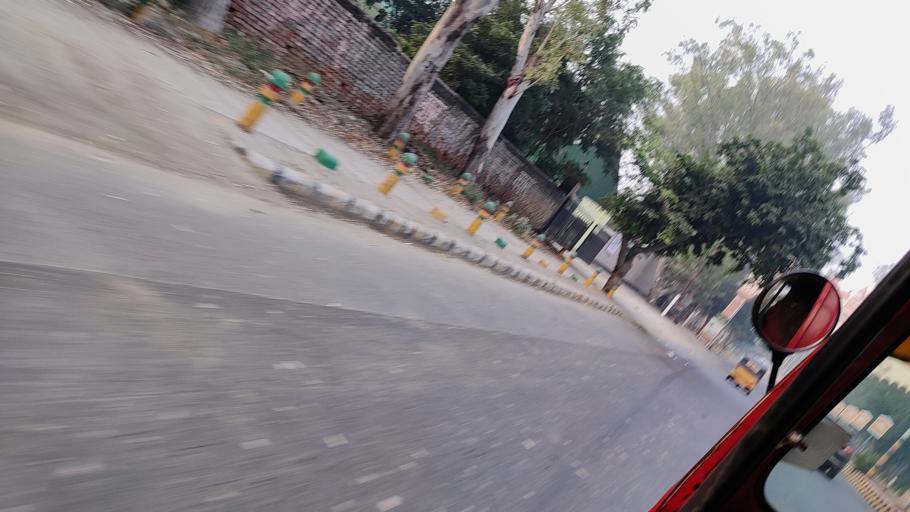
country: IN
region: Uttar Pradesh
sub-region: Mathura
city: Vrindavan
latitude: 27.5662
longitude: 77.6435
